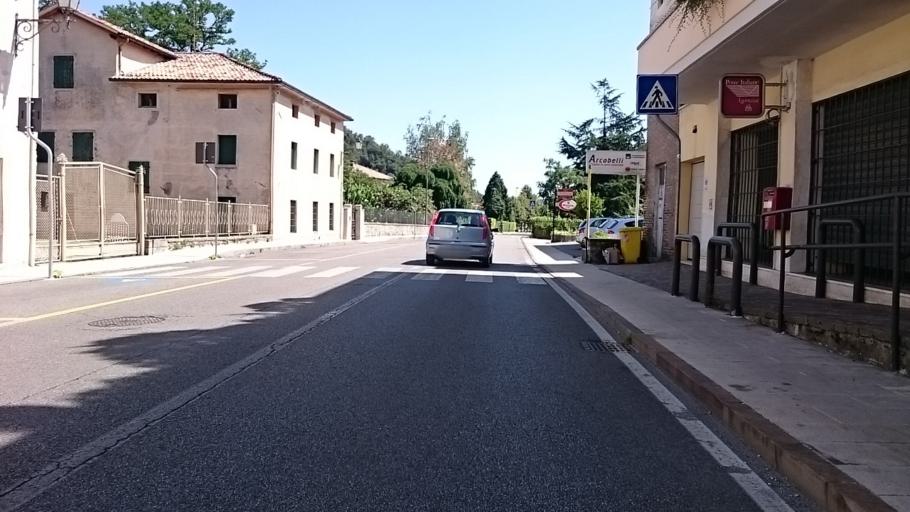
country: IT
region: Veneto
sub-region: Provincia di Treviso
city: Follina
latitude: 45.9510
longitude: 12.1200
